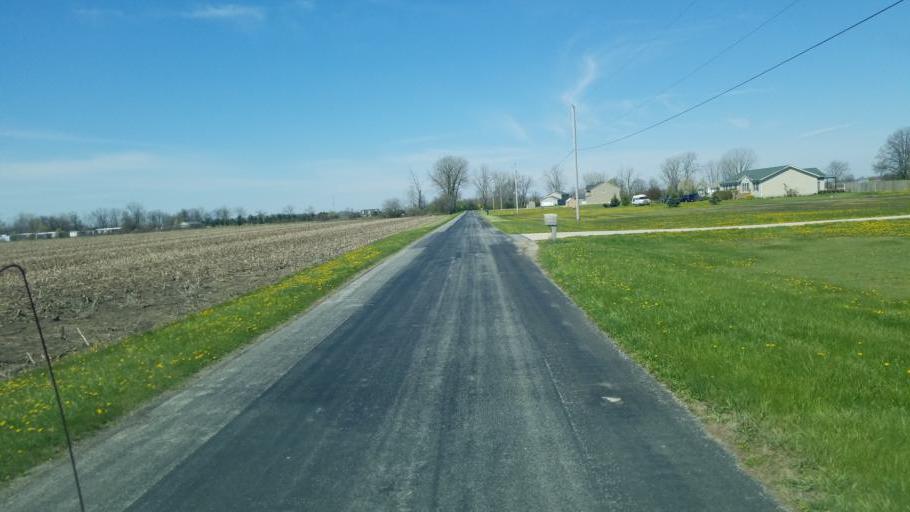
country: US
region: Ohio
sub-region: Marion County
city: Marion
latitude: 40.6355
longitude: -83.0879
